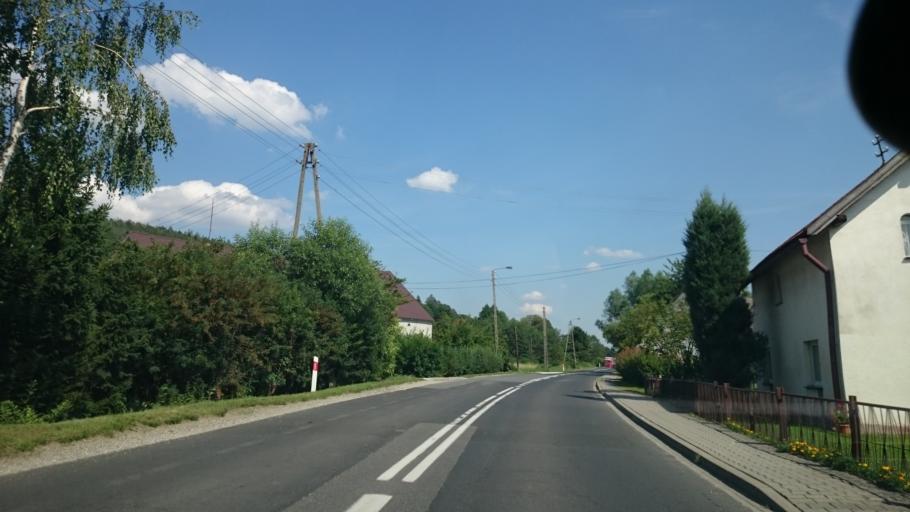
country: PL
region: Lower Silesian Voivodeship
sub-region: Powiat klodzki
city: Bystrzyca Klodzka
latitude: 50.3553
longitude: 16.7388
